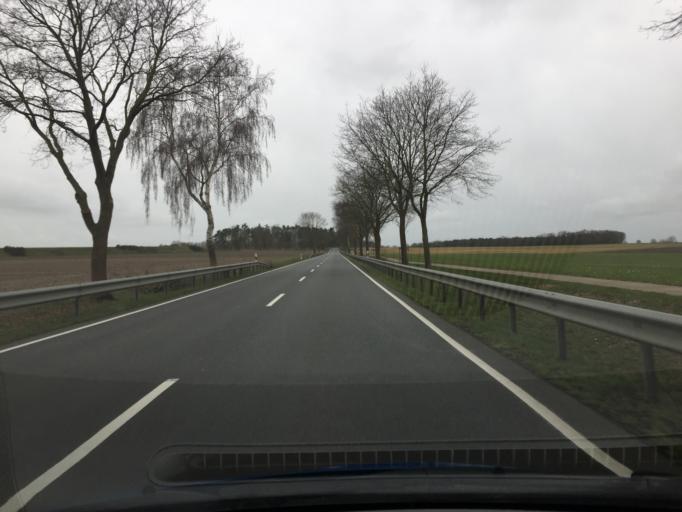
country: DE
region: Lower Saxony
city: Rosche
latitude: 53.0226
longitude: 10.7480
